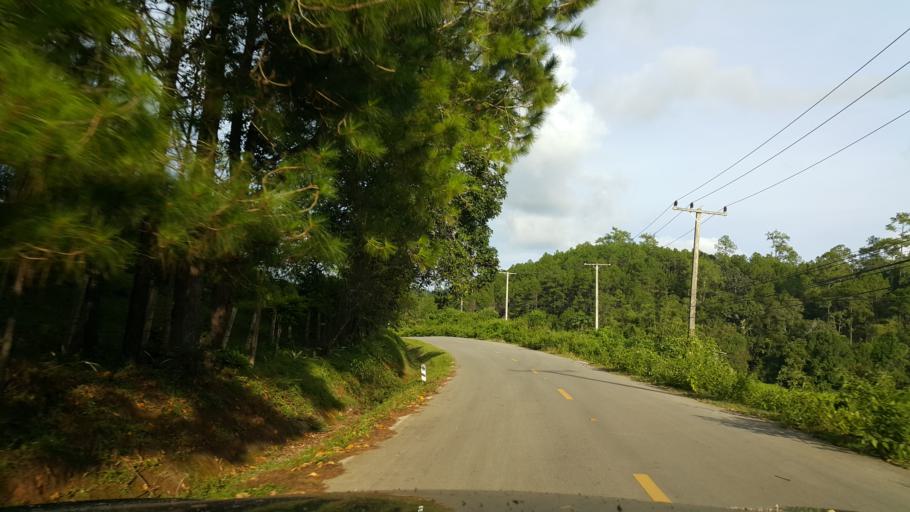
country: TH
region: Chiang Mai
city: Chaem Luang
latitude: 19.0793
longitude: 98.3329
